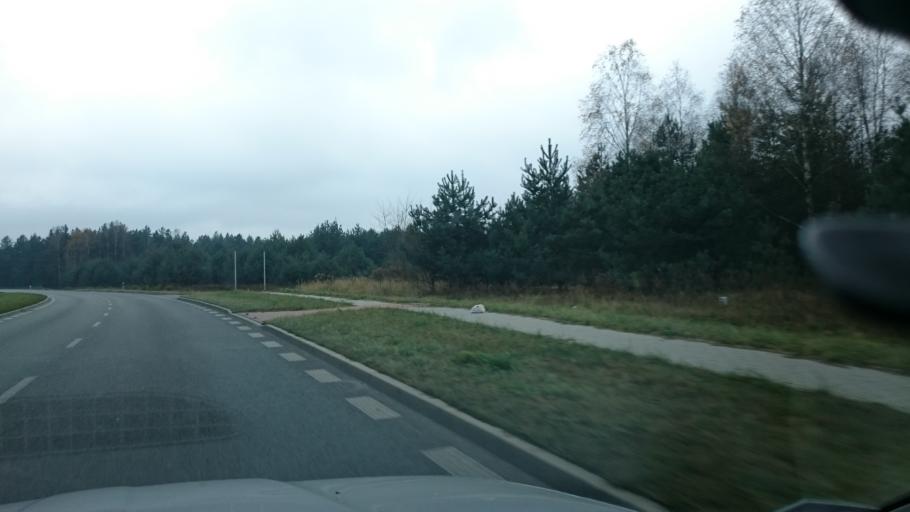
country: PL
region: Swietokrzyskie
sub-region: Powiat konecki
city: Konskie
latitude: 51.1530
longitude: 20.3625
